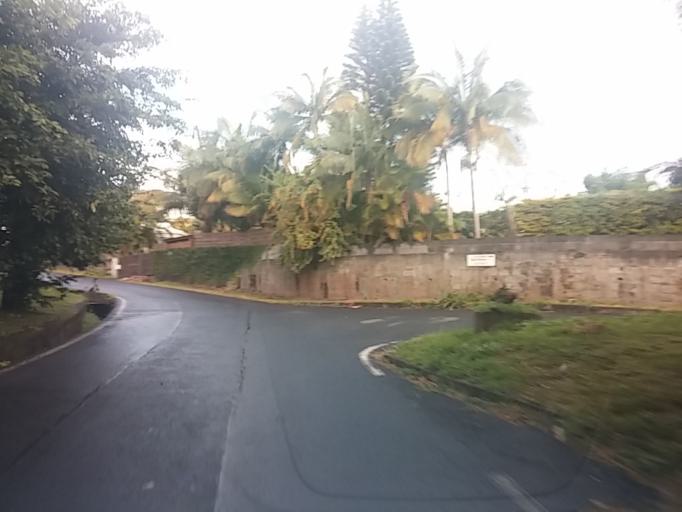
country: RE
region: Reunion
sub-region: Reunion
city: Saint-Denis
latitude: -20.8970
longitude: 55.4118
